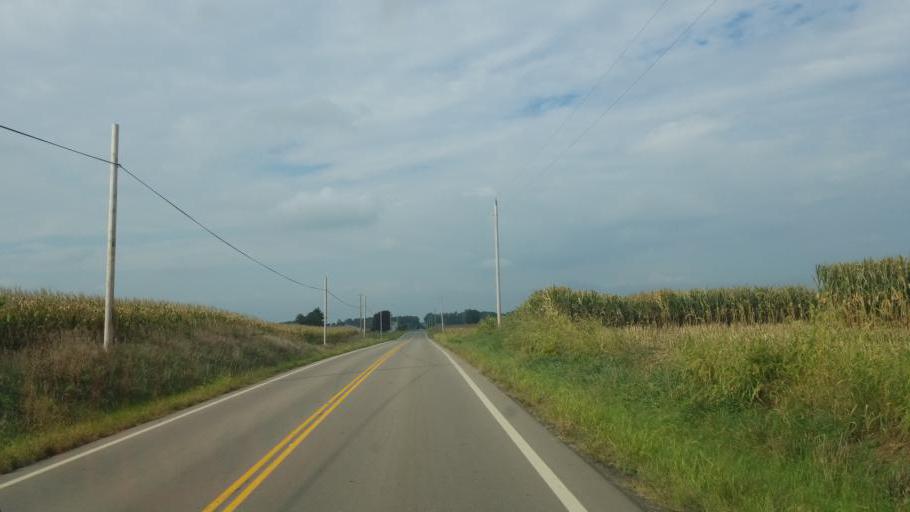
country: US
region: Ohio
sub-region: Wayne County
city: West Salem
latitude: 40.8765
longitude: -82.0535
